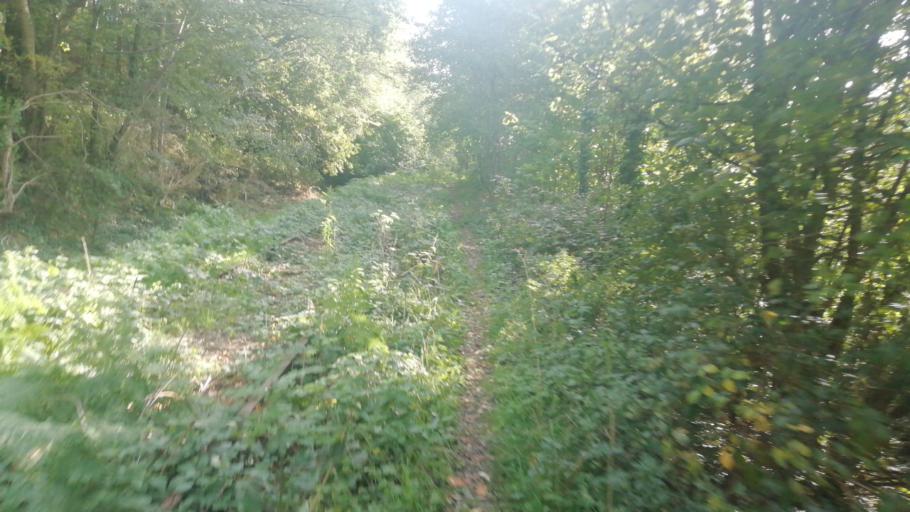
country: FR
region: Haute-Normandie
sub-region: Departement de la Seine-Maritime
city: Rolleville
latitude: 49.5914
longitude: 0.2127
